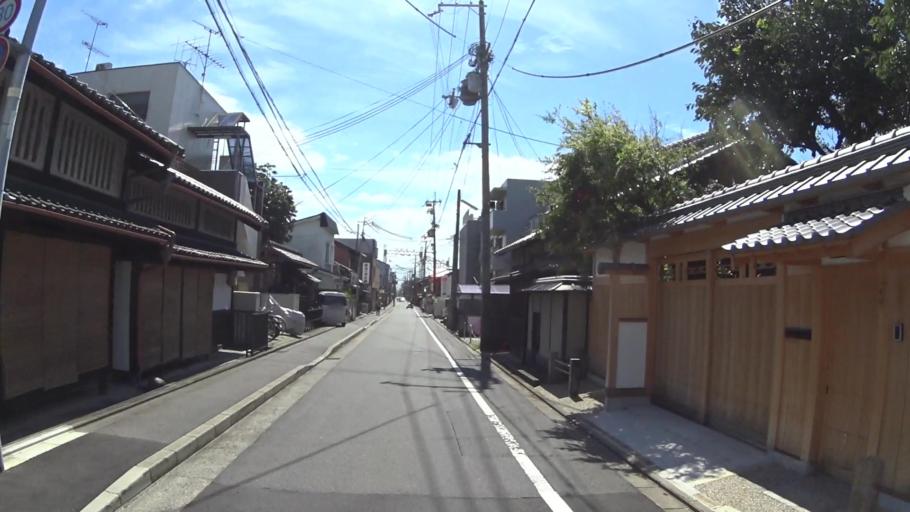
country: JP
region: Kyoto
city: Uji
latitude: 34.9375
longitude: 135.7649
